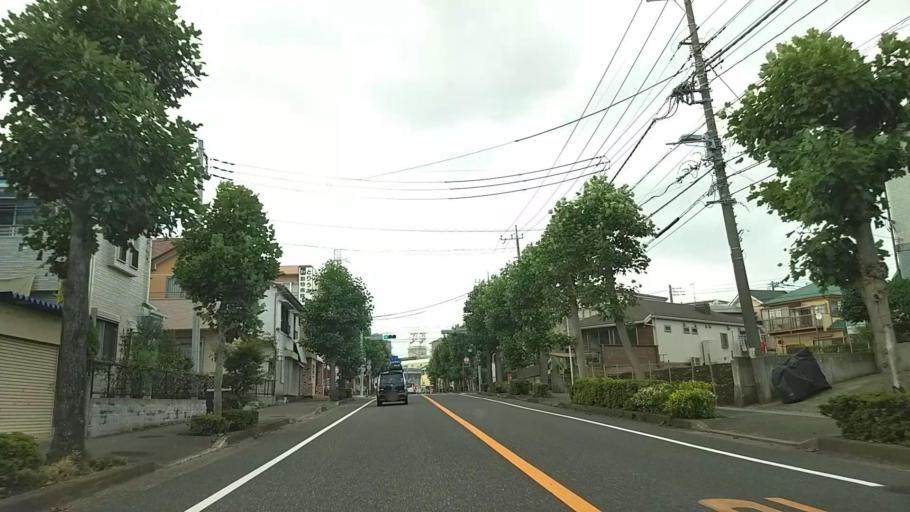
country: JP
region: Kanagawa
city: Isehara
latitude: 35.3909
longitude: 139.3145
